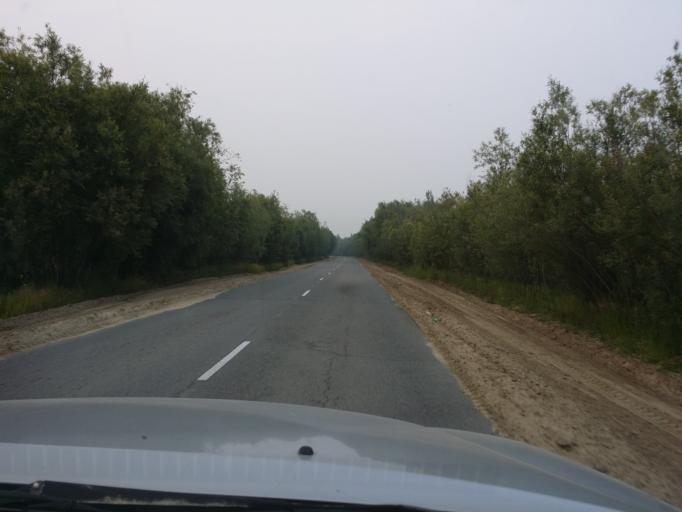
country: RU
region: Khanty-Mansiyskiy Avtonomnyy Okrug
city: Megion
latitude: 60.9903
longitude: 76.2997
